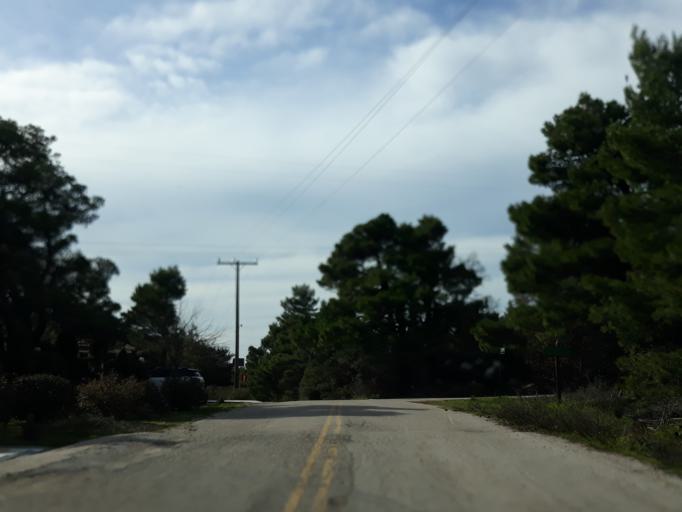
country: GR
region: Attica
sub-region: Nomarchia Anatolikis Attikis
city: Afidnes
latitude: 38.2148
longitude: 23.7924
